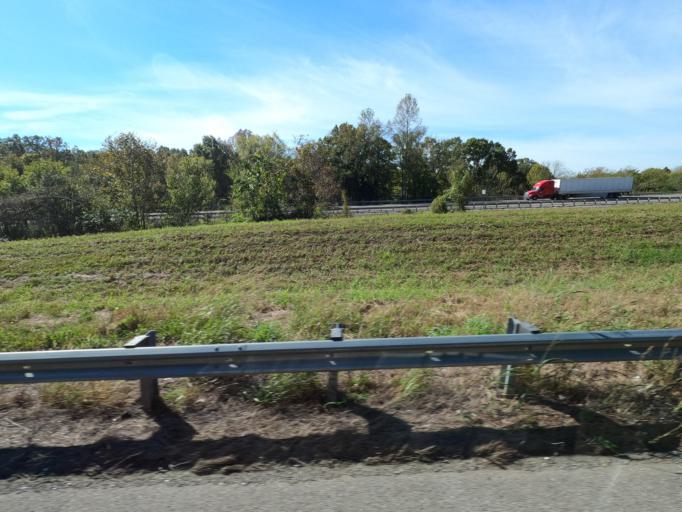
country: US
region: Tennessee
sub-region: Dickson County
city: Burns
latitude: 36.0183
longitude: -87.2526
